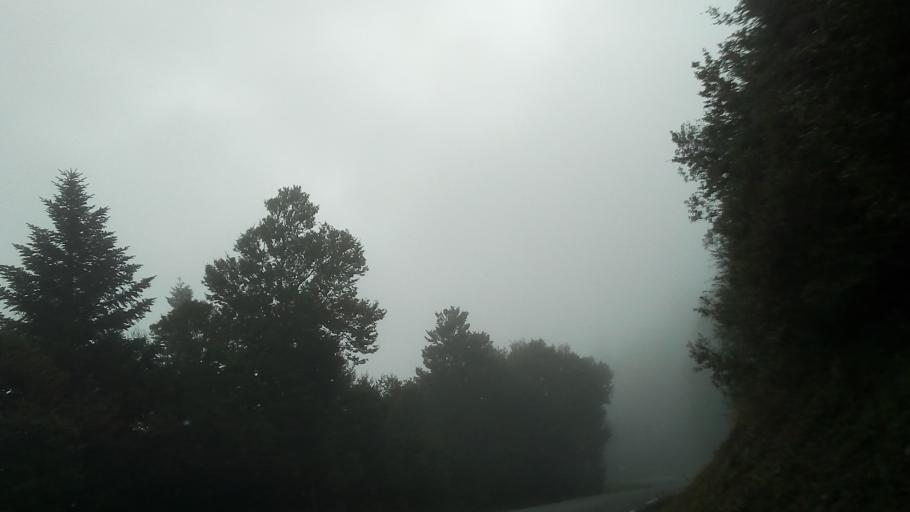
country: FR
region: Midi-Pyrenees
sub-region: Departement des Hautes-Pyrenees
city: Saint-Lary-Soulan
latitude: 42.7853
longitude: 0.1758
